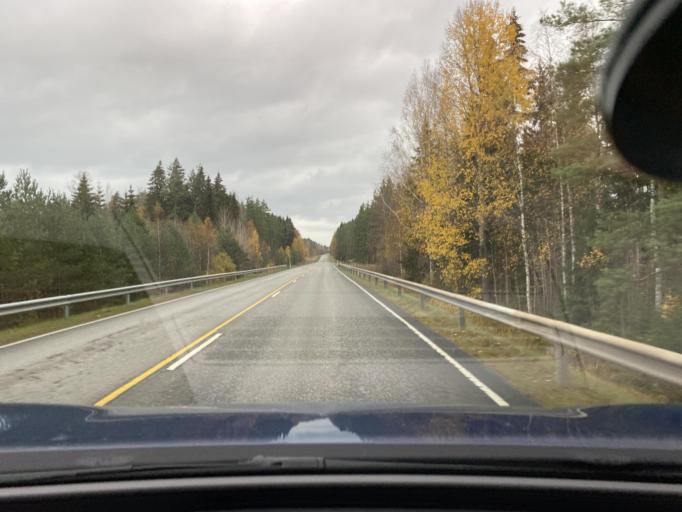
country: FI
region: Varsinais-Suomi
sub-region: Loimaa
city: Ylaene
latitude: 60.8929
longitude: 22.4047
